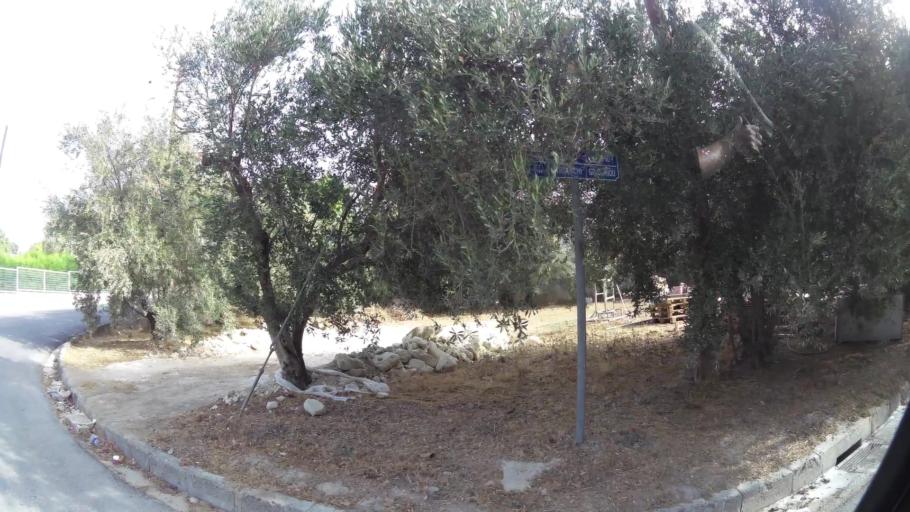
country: CY
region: Lefkosia
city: Geri
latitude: 35.0748
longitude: 33.3888
